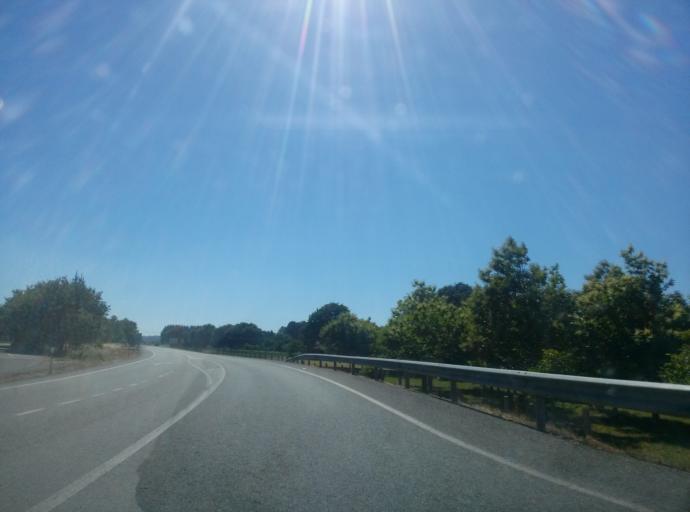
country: ES
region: Galicia
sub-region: Provincia de Lugo
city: Rabade
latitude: 43.1177
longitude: -7.5781
